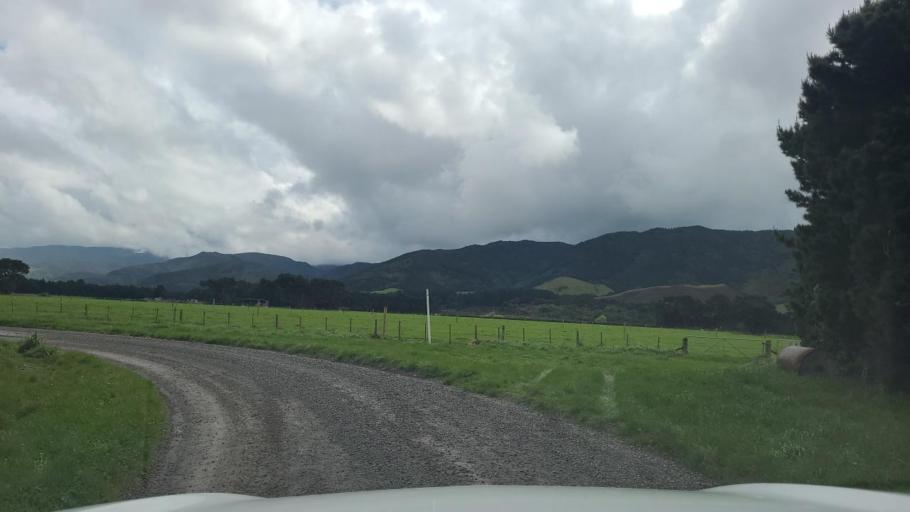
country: NZ
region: Wellington
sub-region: Upper Hutt City
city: Upper Hutt
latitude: -41.1301
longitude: 175.3145
